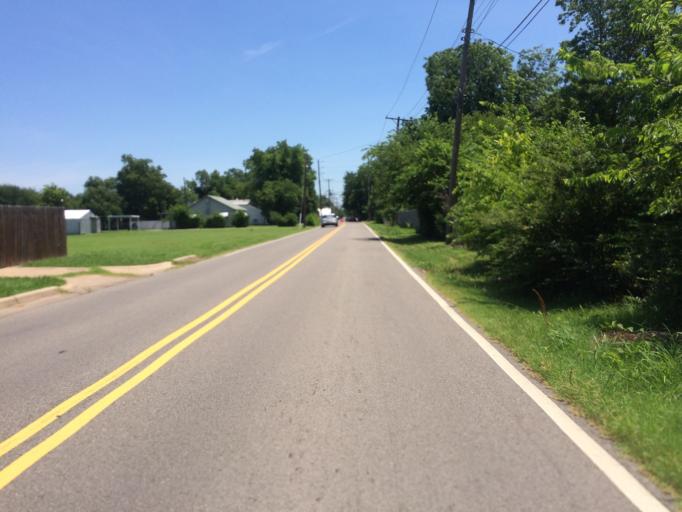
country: US
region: Oklahoma
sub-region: Cleveland County
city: Norman
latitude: 35.2256
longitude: -97.4558
